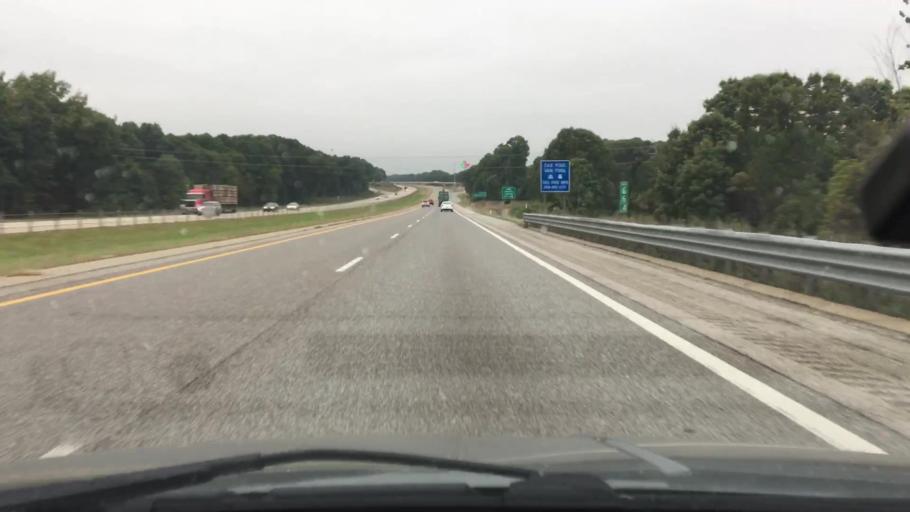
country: US
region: Michigan
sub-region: Van Buren County
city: Mattawan
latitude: 42.2232
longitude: -85.7743
